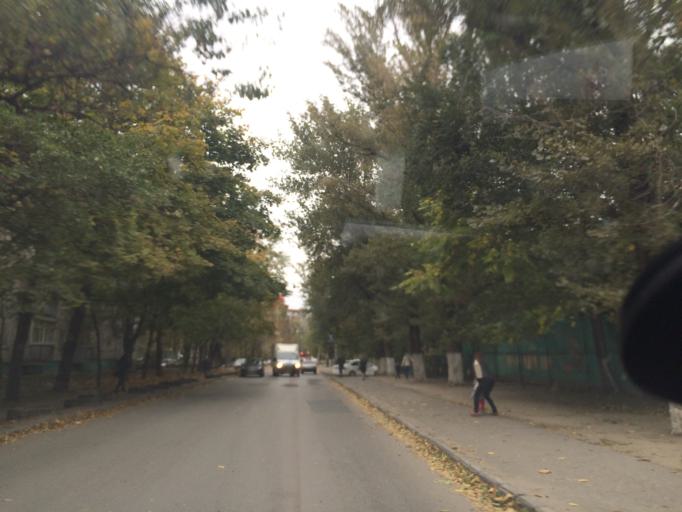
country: RU
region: Rostov
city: Rostov-na-Donu
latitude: 47.2096
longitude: 39.6233
